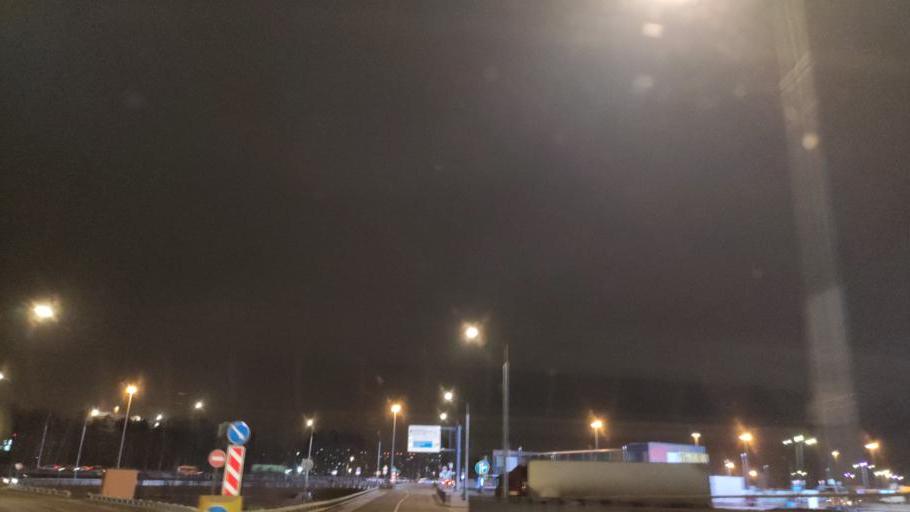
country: RU
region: Moscow
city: Solntsevo
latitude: 55.6239
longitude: 37.4191
